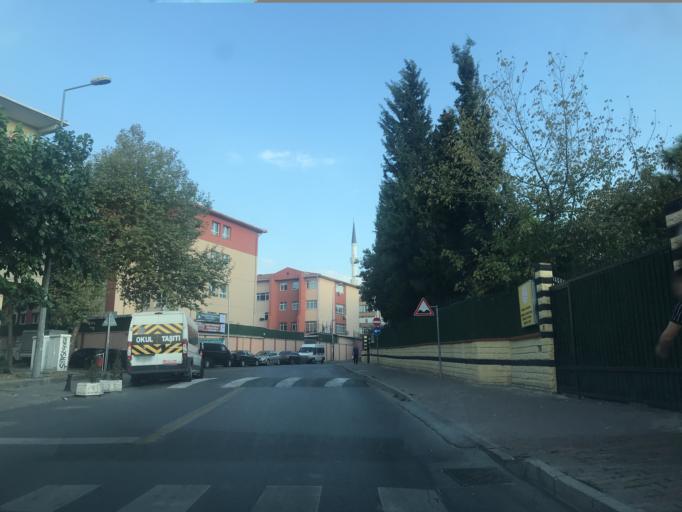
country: TR
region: Istanbul
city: merter keresteciler
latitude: 41.0353
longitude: 28.9171
